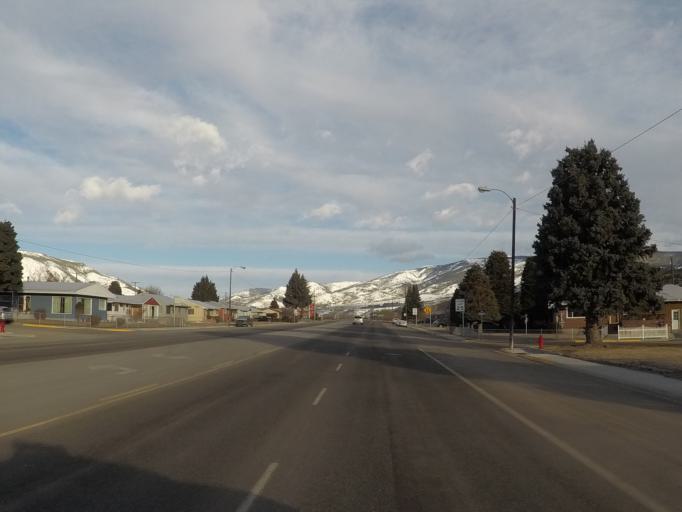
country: US
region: Montana
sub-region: Deer Lodge County
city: Anaconda
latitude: 46.1379
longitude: -112.9810
